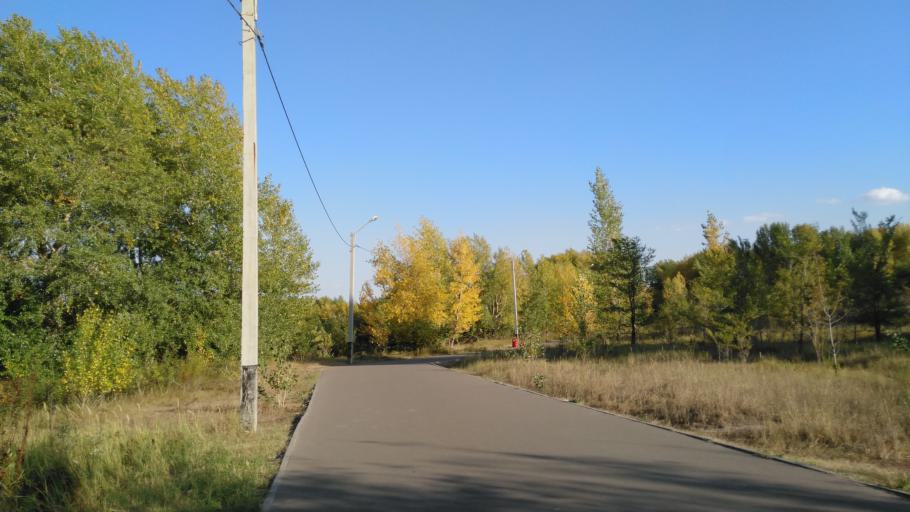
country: KZ
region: Pavlodar
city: Pavlodar
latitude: 52.2620
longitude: 76.9325
